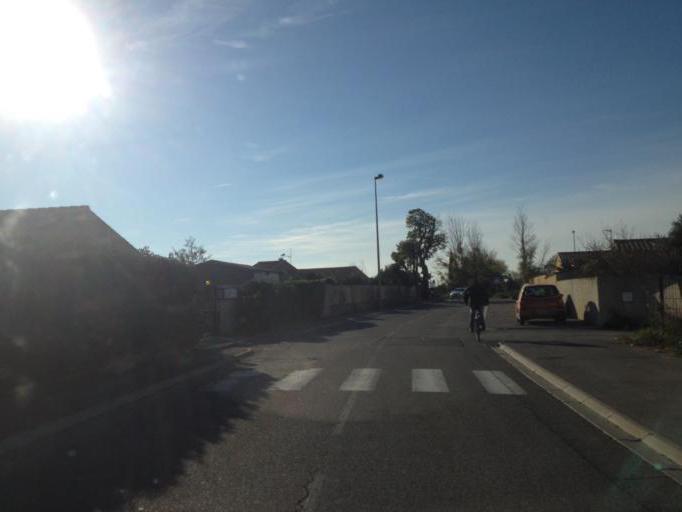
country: FR
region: Provence-Alpes-Cote d'Azur
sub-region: Departement des Bouches-du-Rhone
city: Istres
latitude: 43.5061
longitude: 4.9688
